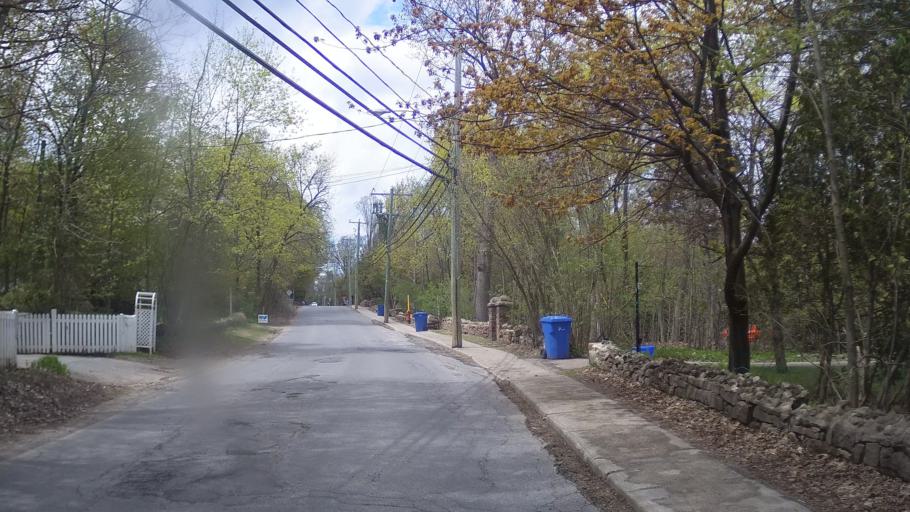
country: CA
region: Quebec
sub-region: Monteregie
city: Hudson
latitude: 45.4633
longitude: -74.1483
